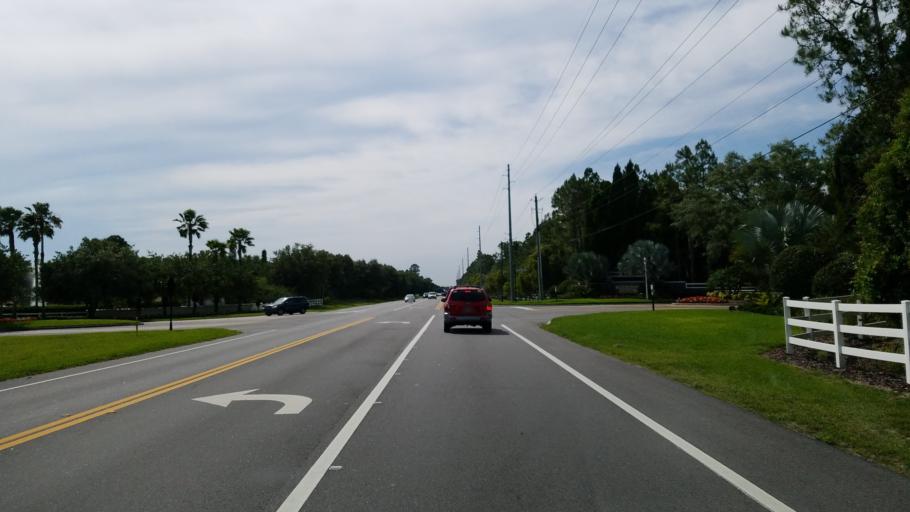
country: US
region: Florida
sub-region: Hillsborough County
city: Fish Hawk
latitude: 27.8568
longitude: -82.1918
